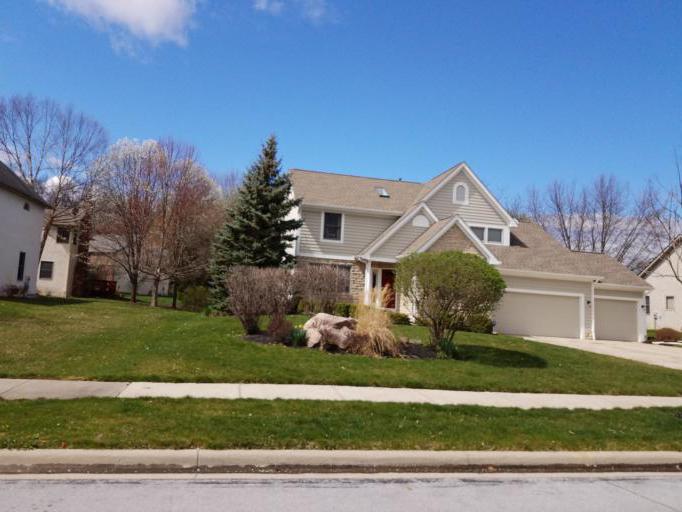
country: US
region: Ohio
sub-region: Franklin County
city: Westerville
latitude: 40.1445
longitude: -82.8900
